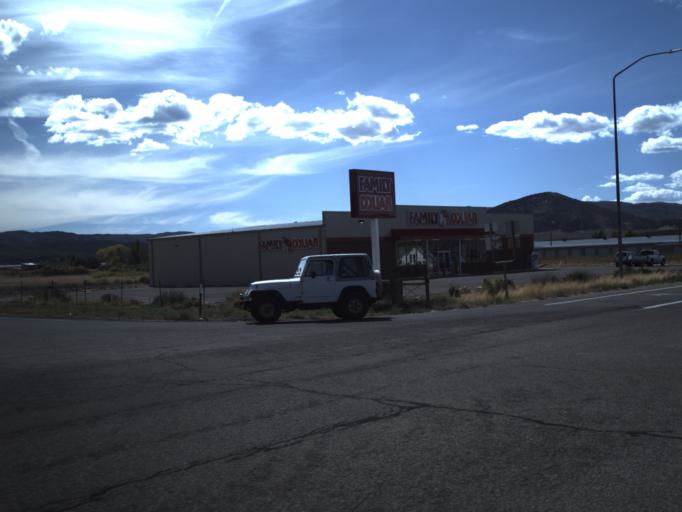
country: US
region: Utah
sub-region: Washington County
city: Enterprise
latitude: 37.5738
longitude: -113.7044
